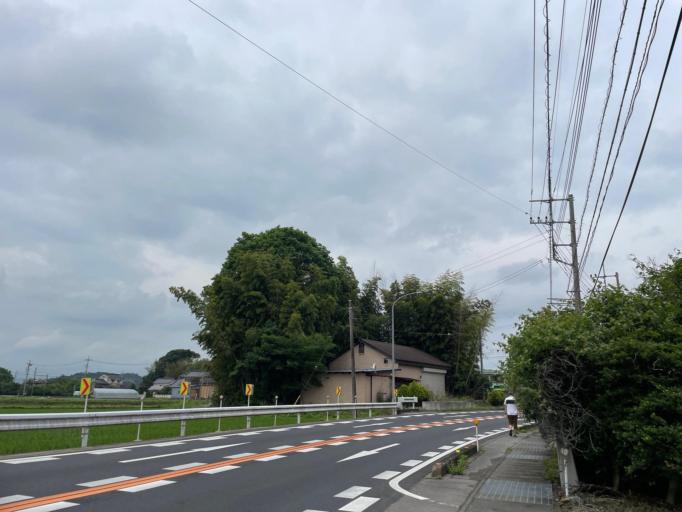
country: JP
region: Tochigi
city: Kanuma
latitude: 36.4840
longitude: 139.7496
